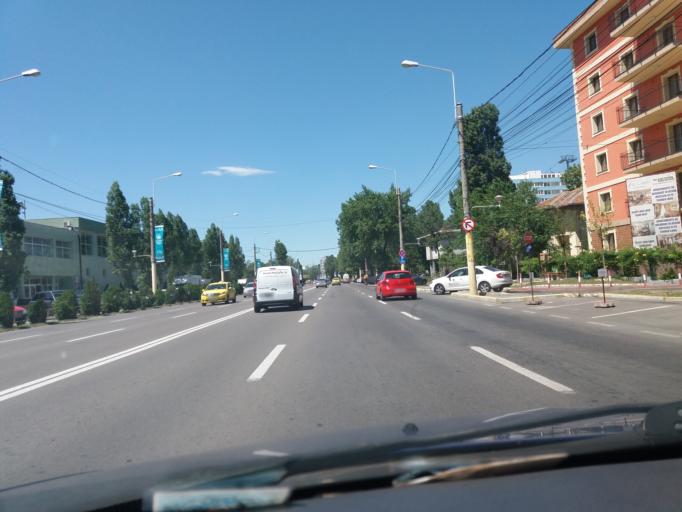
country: RO
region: Constanta
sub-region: Municipiul Constanta
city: Palazu Mare
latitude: 44.2290
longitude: 28.6266
